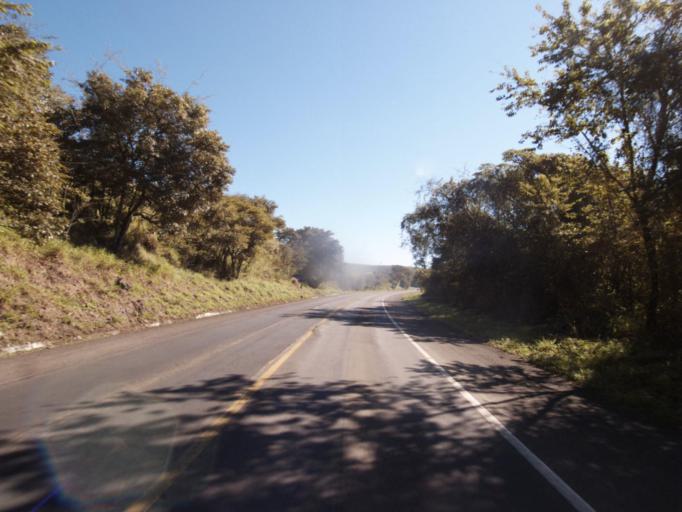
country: BR
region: Rio Grande do Sul
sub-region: Frederico Westphalen
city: Frederico Westphalen
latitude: -26.8248
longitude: -53.4058
